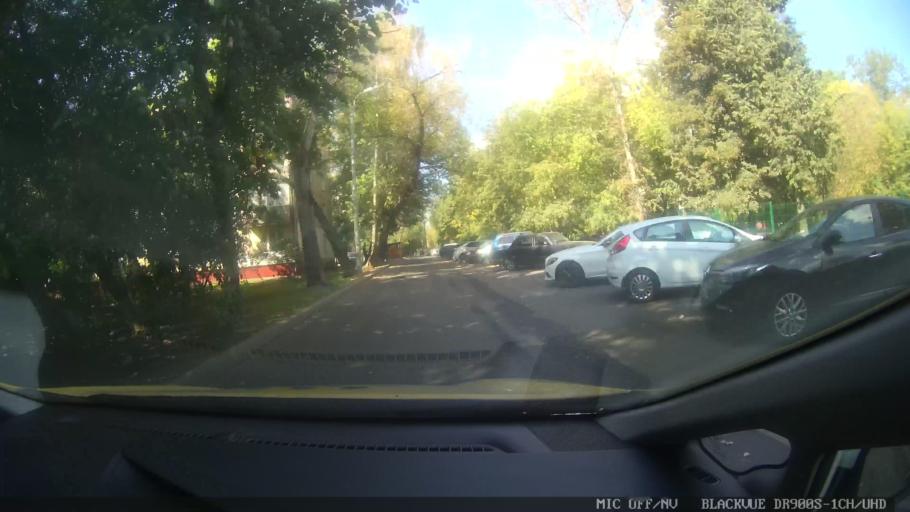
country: RU
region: Moscow
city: Kuz'minki
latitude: 55.6999
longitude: 37.7855
